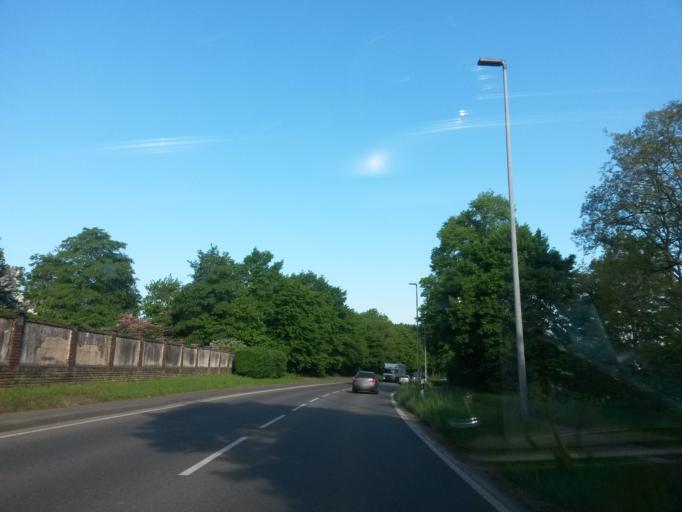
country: DE
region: North Rhine-Westphalia
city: Sankt Augustin
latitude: 50.7758
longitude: 7.1767
